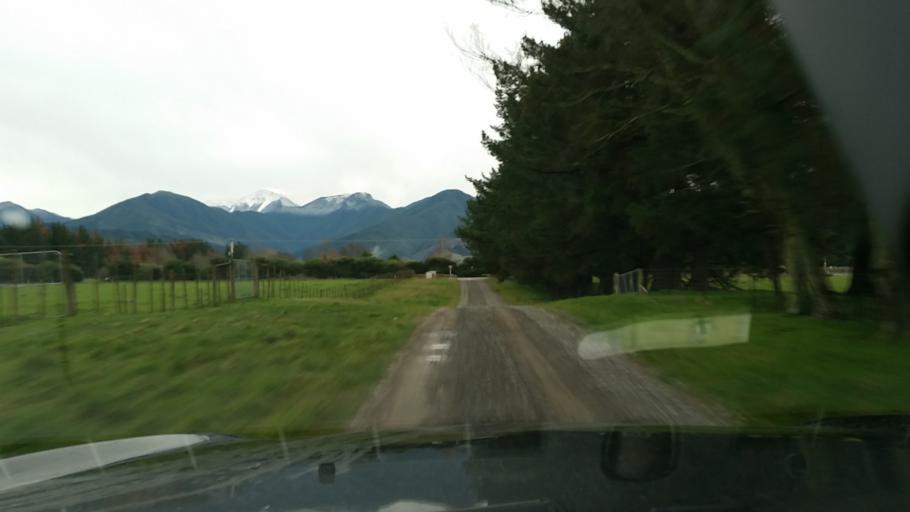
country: NZ
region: Marlborough
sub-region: Marlborough District
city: Blenheim
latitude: -41.5431
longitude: 173.6075
